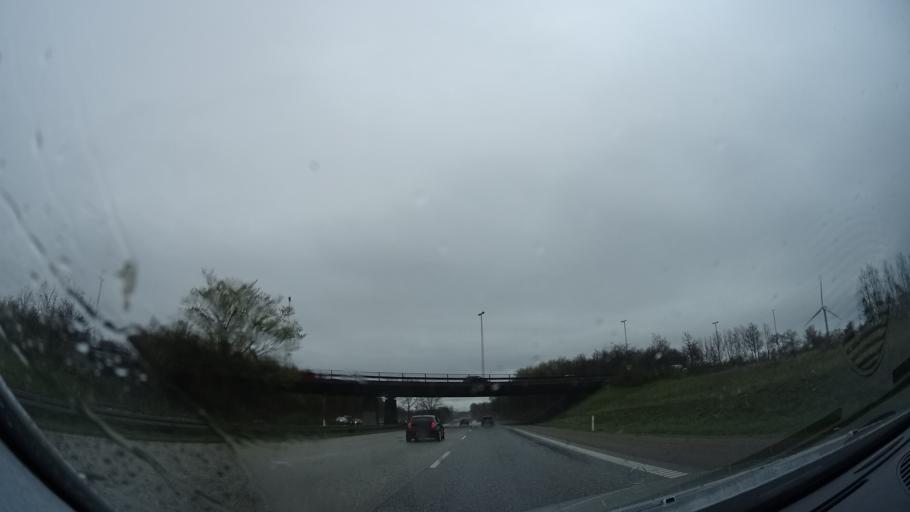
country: DK
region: Capital Region
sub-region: Hoje-Taastrup Kommune
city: Taastrup
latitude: 55.6643
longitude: 12.2792
